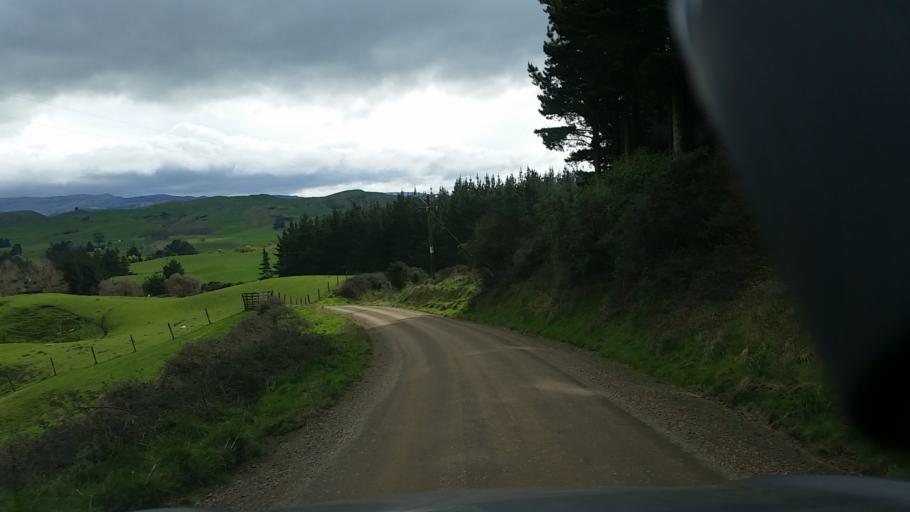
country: NZ
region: Hawke's Bay
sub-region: Napier City
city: Napier
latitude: -39.1906
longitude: 176.9144
